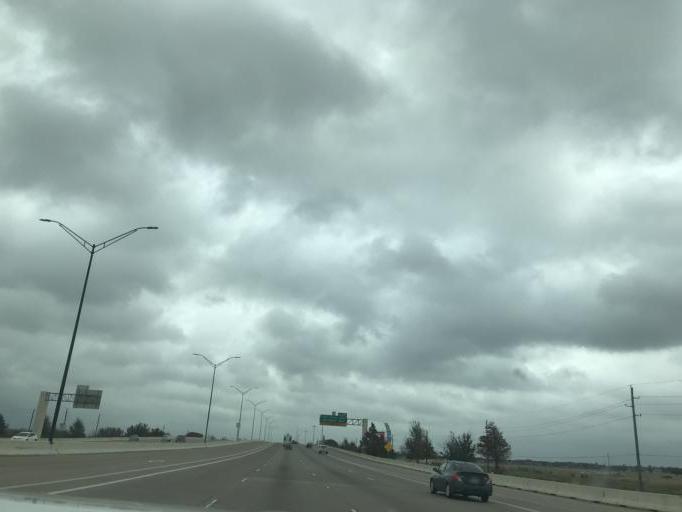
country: US
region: Texas
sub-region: Fort Bend County
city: New Territory
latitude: 29.5785
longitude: -95.6515
